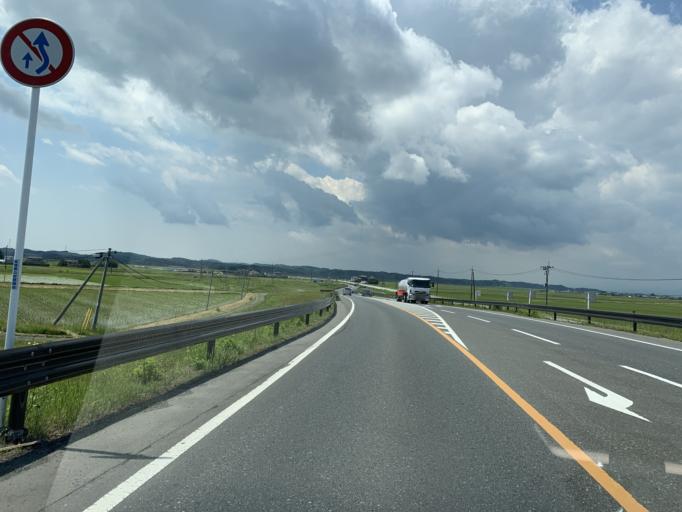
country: JP
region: Miyagi
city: Matsushima
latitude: 38.4544
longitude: 141.0863
